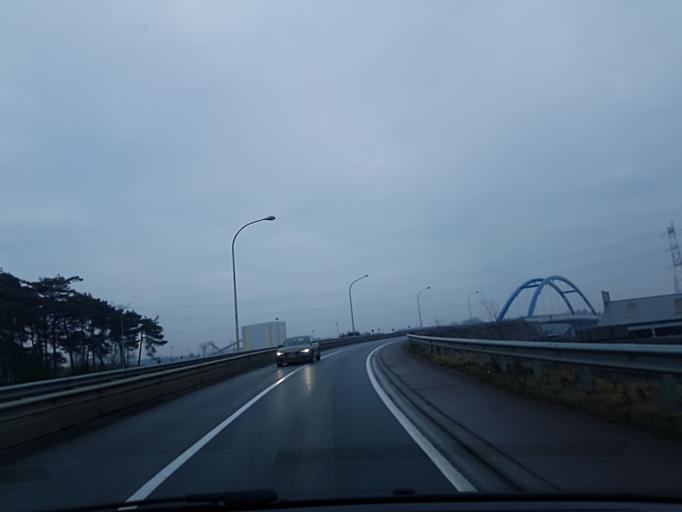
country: BE
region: Flanders
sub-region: Provincie Antwerpen
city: Grobbendonk
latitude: 51.1820
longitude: 4.7447
